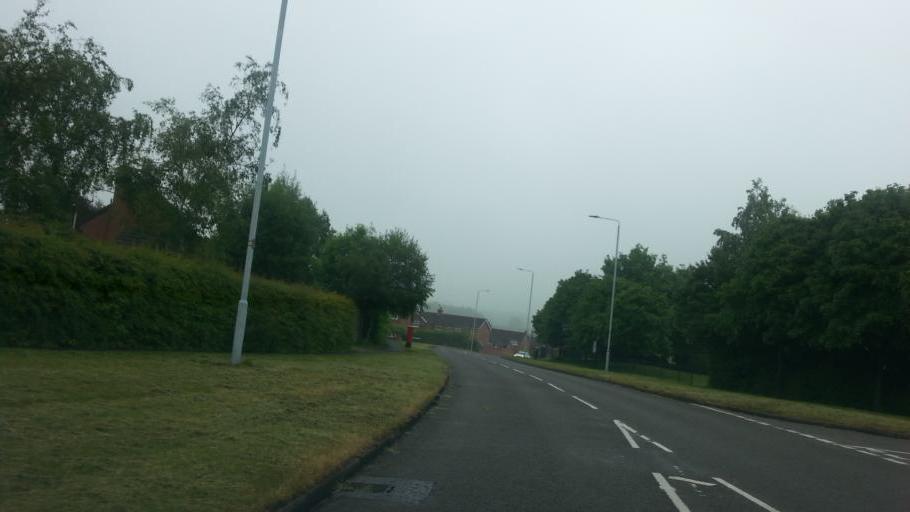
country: GB
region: England
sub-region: Leicestershire
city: Great Glen
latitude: 52.5910
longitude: -1.0557
